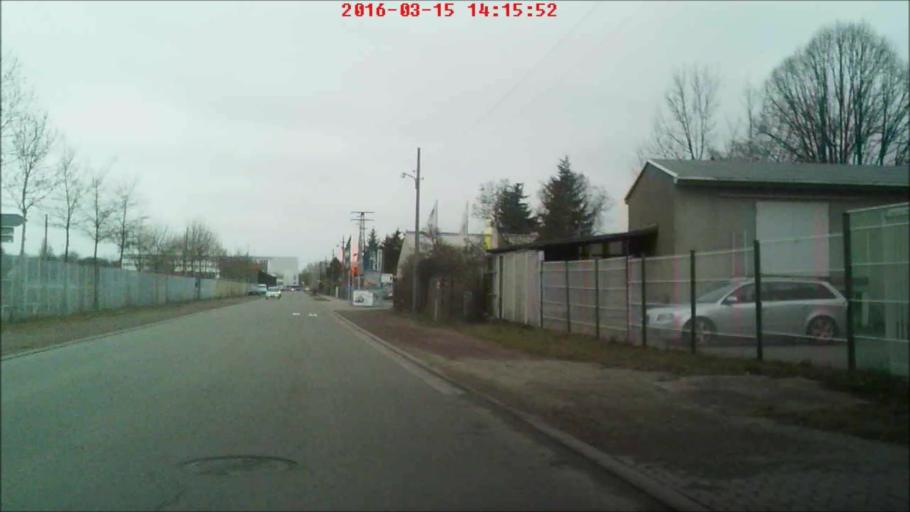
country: DE
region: Thuringia
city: Arnstadt
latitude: 50.8395
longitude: 10.9606
